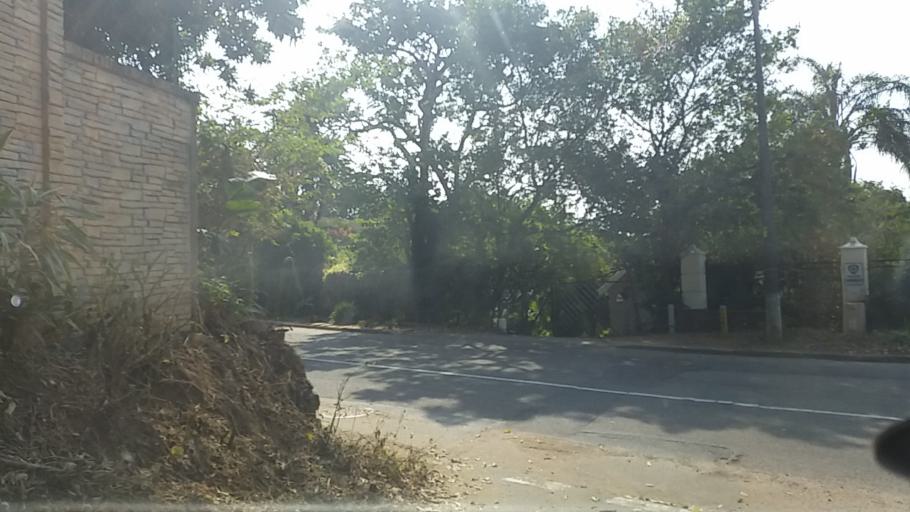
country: ZA
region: KwaZulu-Natal
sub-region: eThekwini Metropolitan Municipality
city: Berea
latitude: -29.8361
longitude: 30.9304
